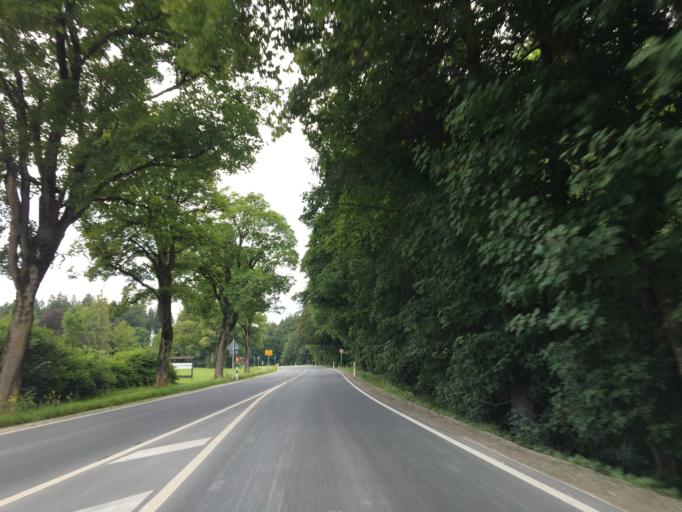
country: DE
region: Bavaria
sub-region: Upper Bavaria
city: Holzkirchen
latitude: 47.8890
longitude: 11.6848
